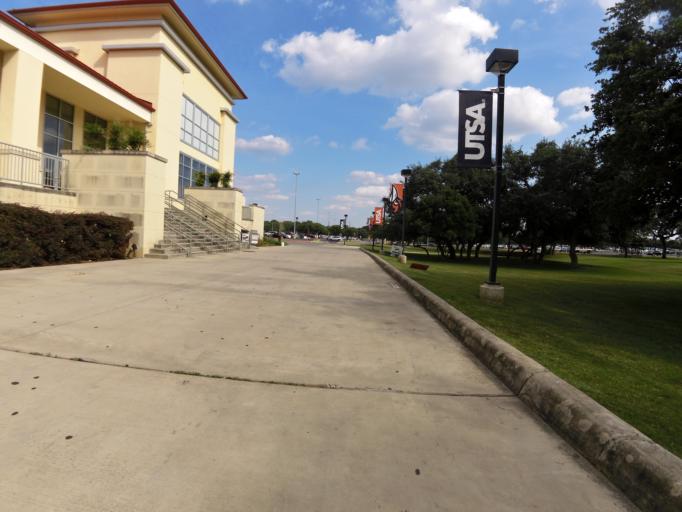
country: US
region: Texas
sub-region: Bexar County
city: Shavano Park
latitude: 29.5828
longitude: -98.6202
